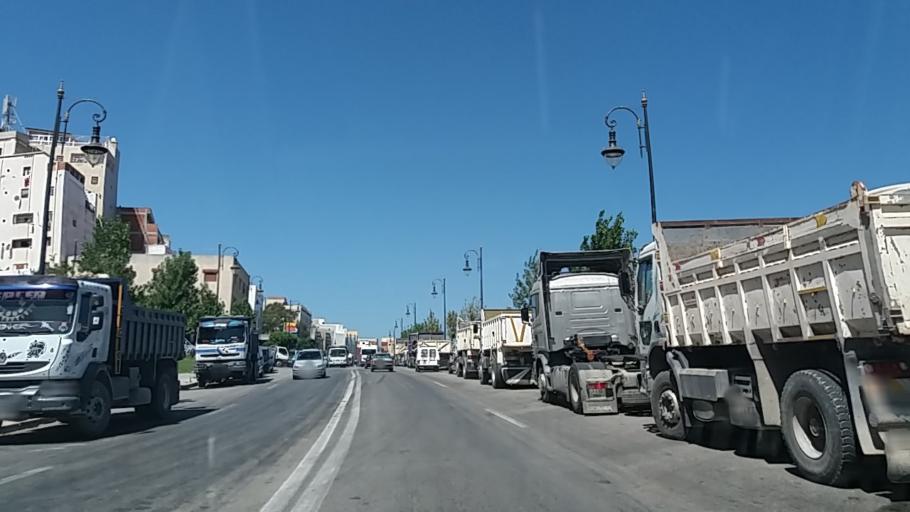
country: MA
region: Tanger-Tetouan
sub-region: Tanger-Assilah
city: Tangier
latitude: 35.7716
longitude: -5.7660
